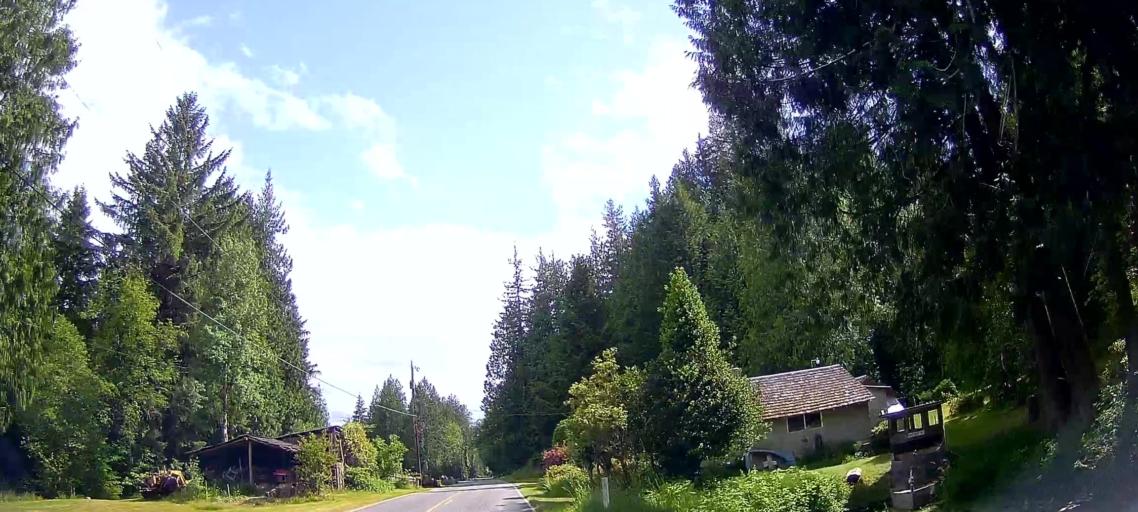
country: US
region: Washington
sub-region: Skagit County
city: Sedro-Woolley
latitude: 48.5516
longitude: -122.2128
